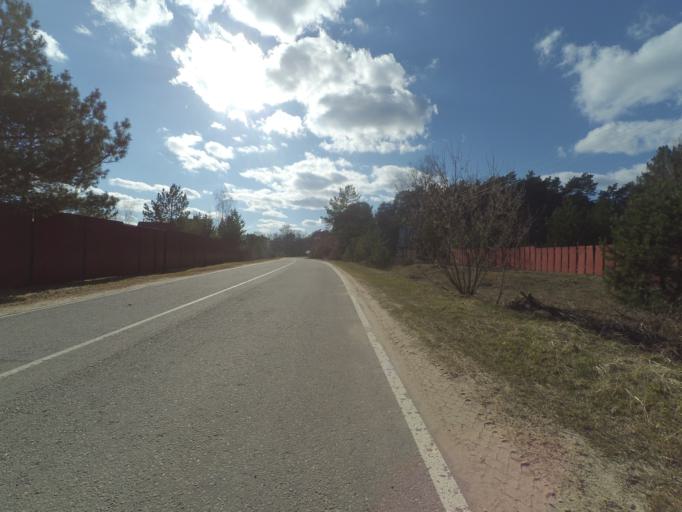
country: RU
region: Moskovskaya
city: Stupino
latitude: 54.8525
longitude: 37.8784
